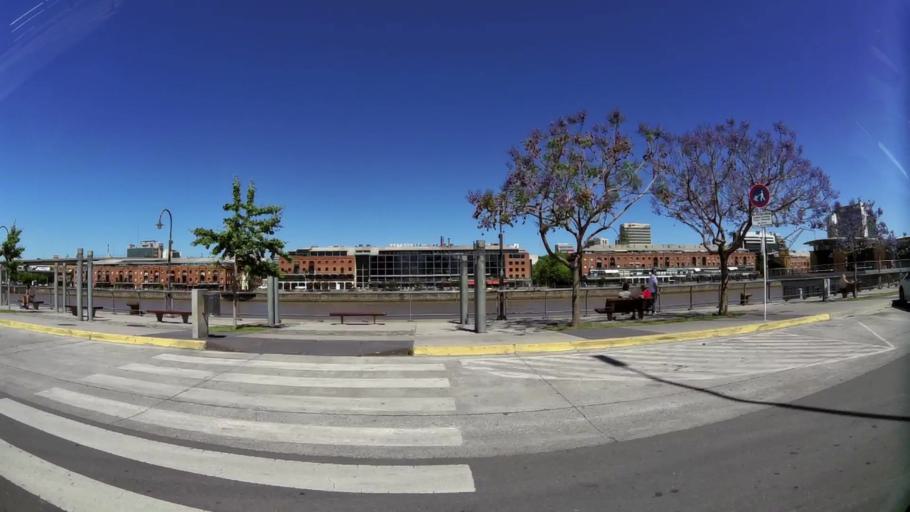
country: AR
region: Buenos Aires F.D.
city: Buenos Aires
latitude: -34.6213
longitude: -58.3625
